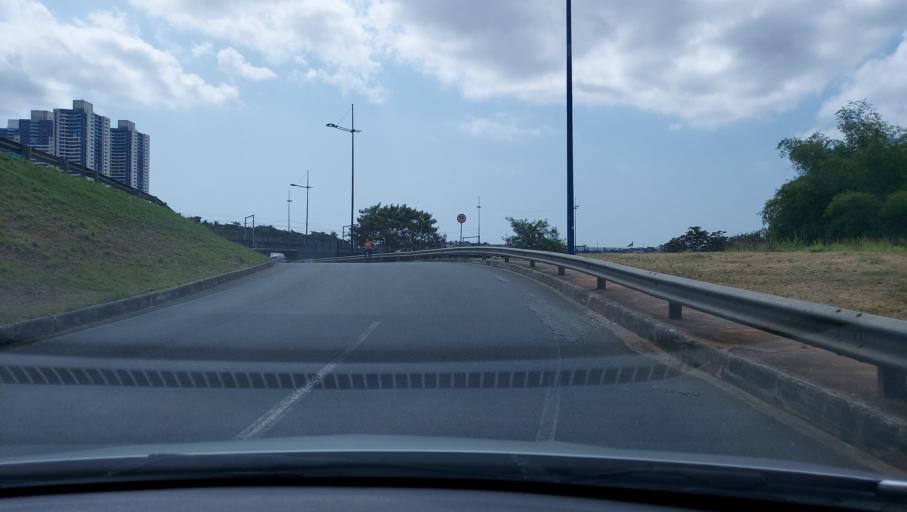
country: BR
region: Bahia
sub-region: Salvador
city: Salvador
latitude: -12.9724
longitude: -38.4759
